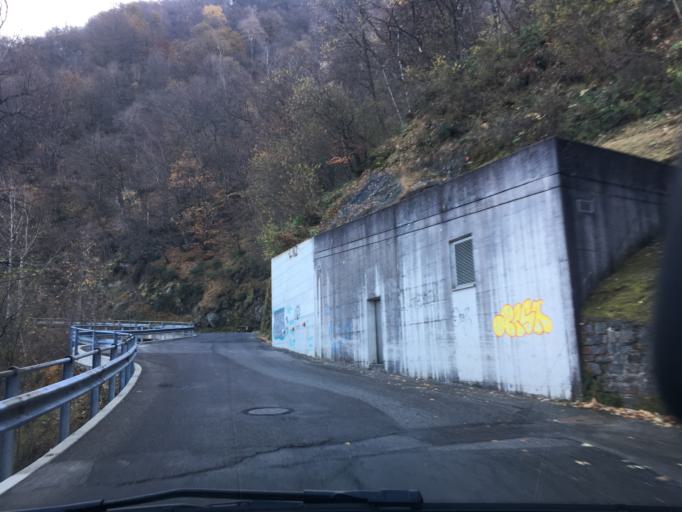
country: CH
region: Ticino
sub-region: Locarno District
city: Magadino
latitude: 46.1269
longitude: 8.8389
